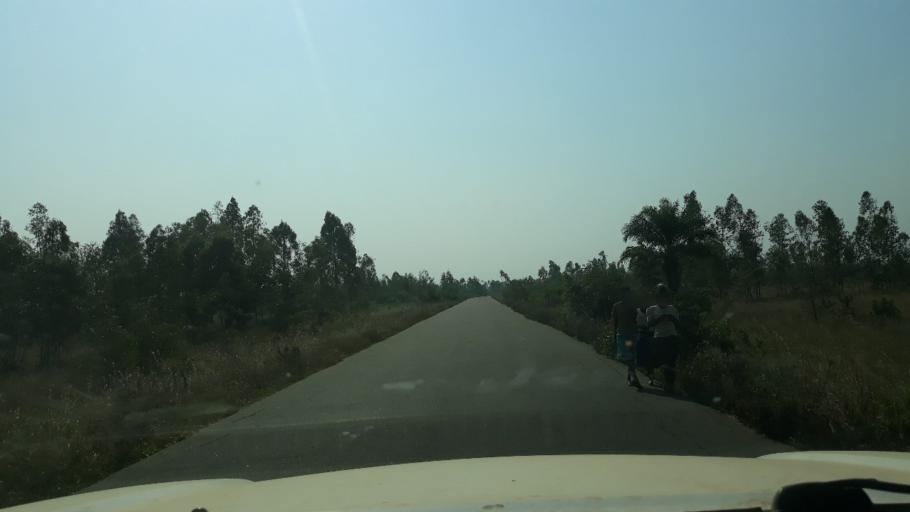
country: BI
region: Cibitoke
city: Cibitoke
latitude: -2.9521
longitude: 29.0733
